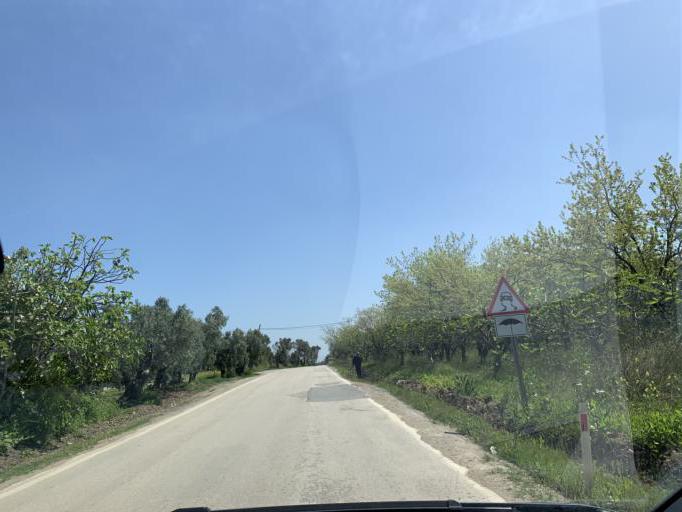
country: TR
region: Bursa
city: Niluefer
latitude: 40.3537
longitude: 28.9517
